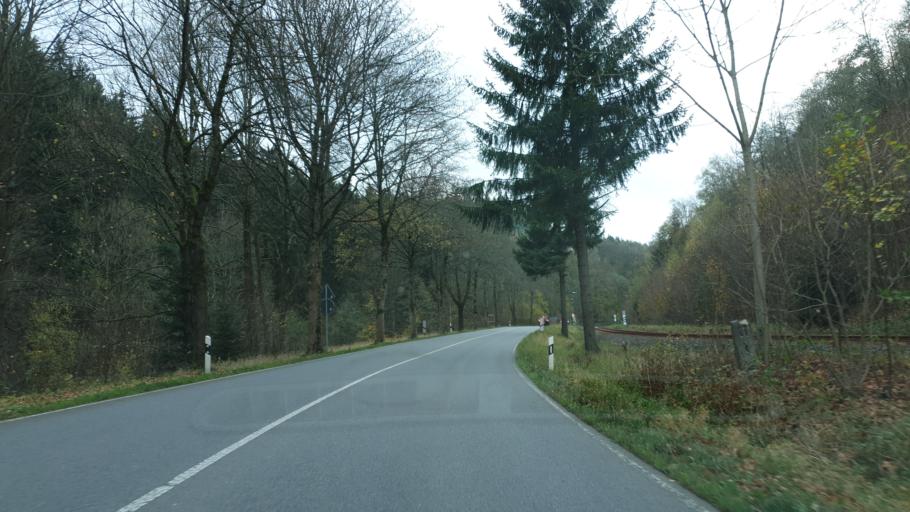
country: DE
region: Saxony
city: Breitenbrunn
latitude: 50.5028
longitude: 12.7635
